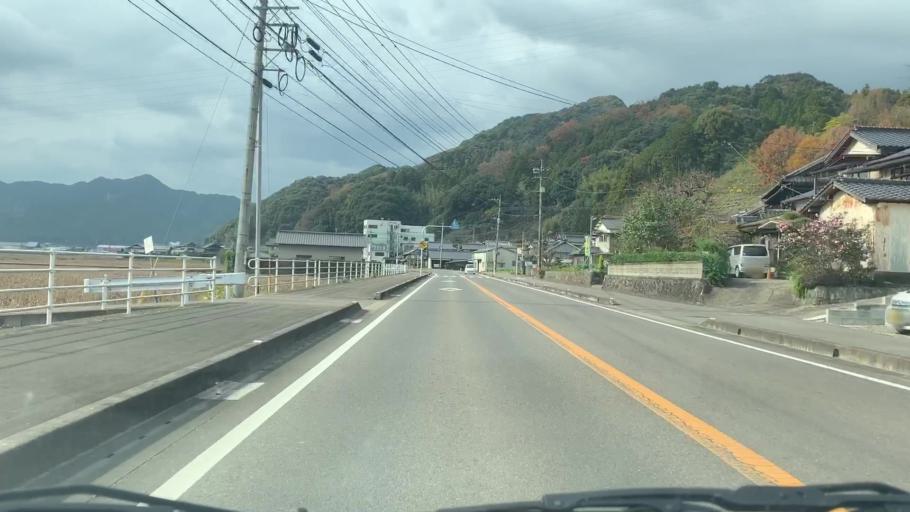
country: JP
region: Saga Prefecture
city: Kashima
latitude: 33.1283
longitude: 130.0546
